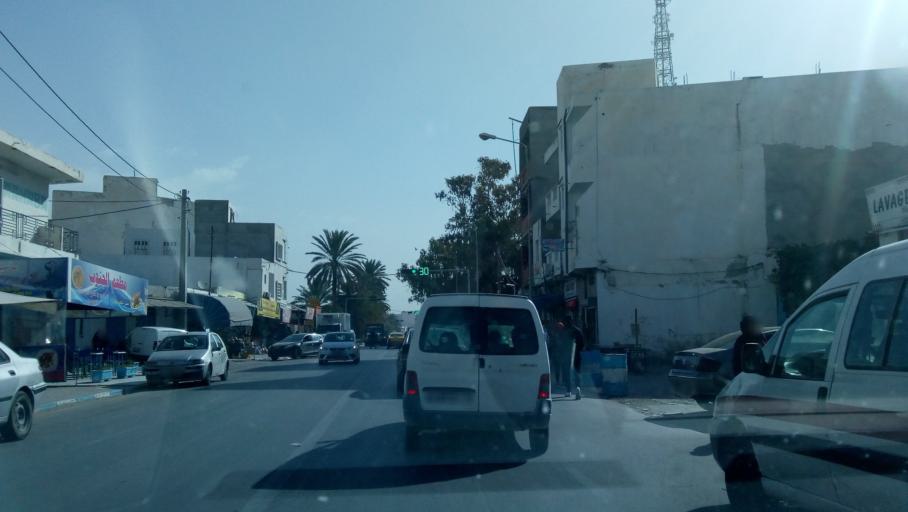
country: TN
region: Qabis
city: Gabes
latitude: 33.8849
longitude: 10.0907
